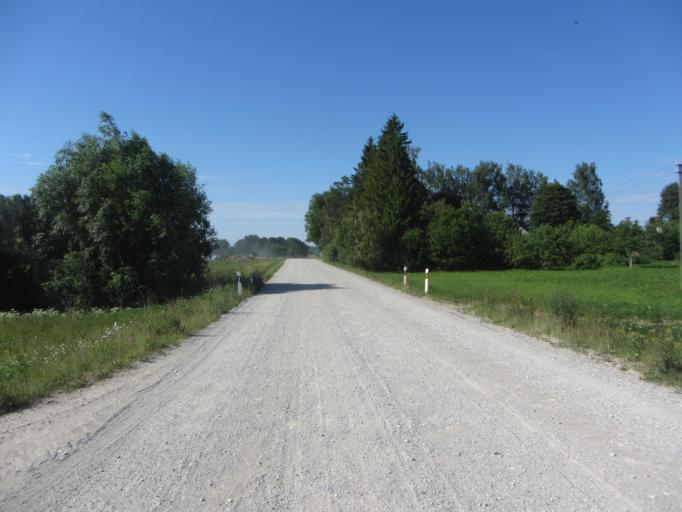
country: LT
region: Panevezys
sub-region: Birzai
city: Birzai
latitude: 56.3620
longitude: 24.6334
